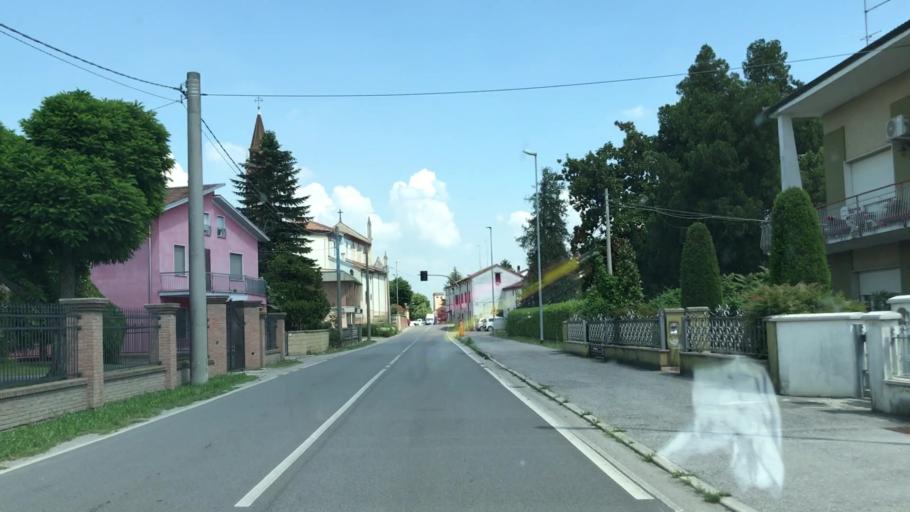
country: IT
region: Lombardy
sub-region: Provincia di Mantova
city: Dosolo
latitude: 45.0169
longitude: 10.6241
